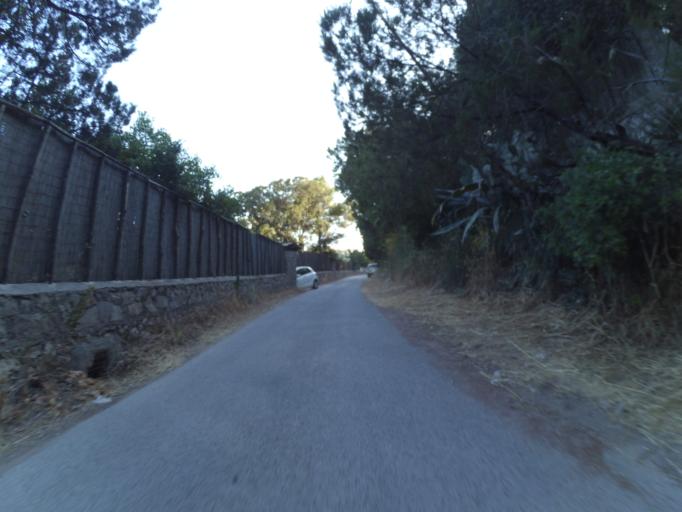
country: IT
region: Latium
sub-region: Provincia di Latina
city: San Felice Circeo
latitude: 41.2236
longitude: 13.0746
